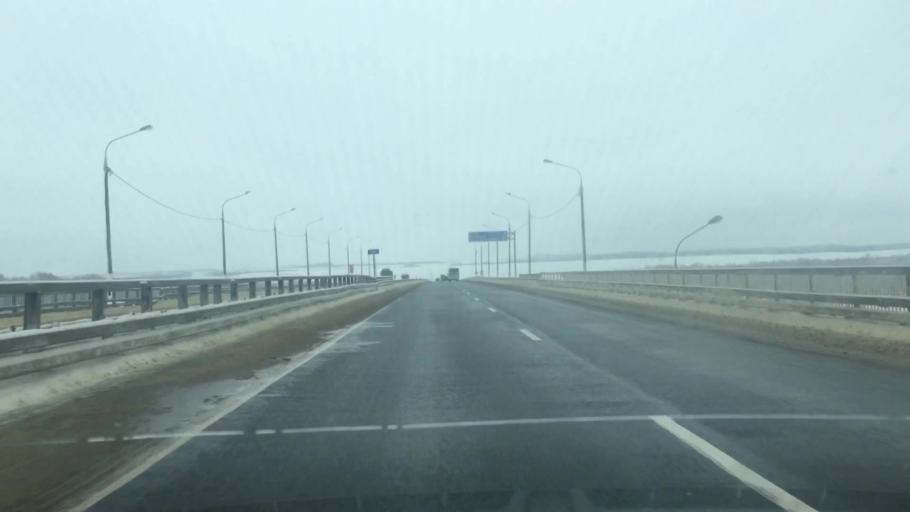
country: RU
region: Tula
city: Kazachka
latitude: 53.2885
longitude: 38.1787
